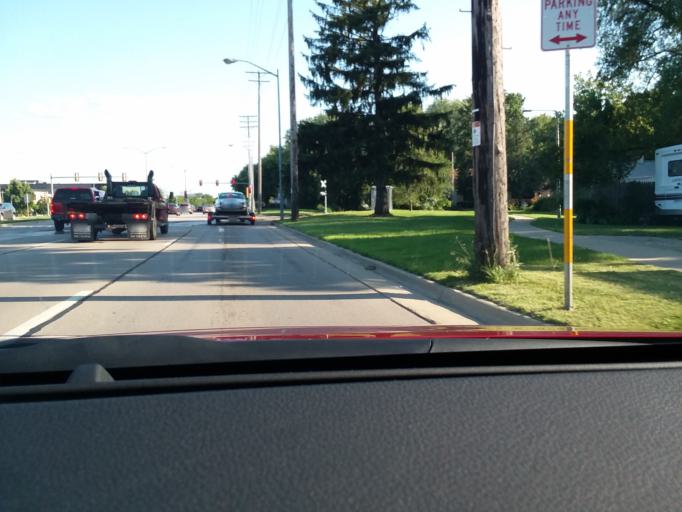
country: US
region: Wisconsin
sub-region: Dane County
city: Maple Bluff
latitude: 43.1227
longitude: -89.3552
